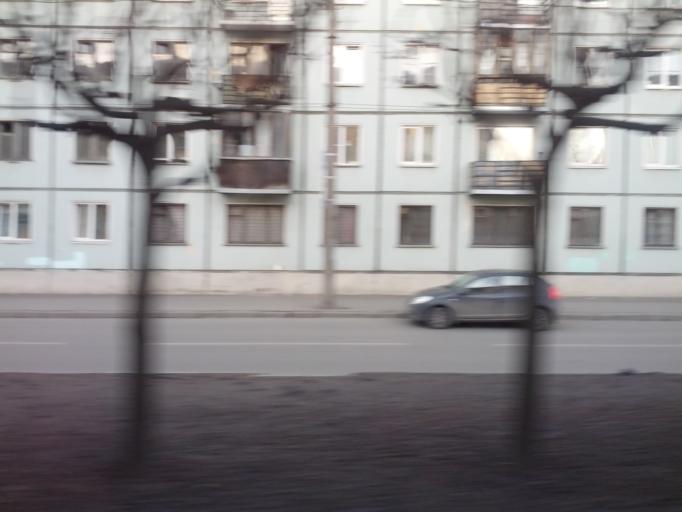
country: RU
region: St.-Petersburg
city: Centralniy
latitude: 59.9215
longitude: 30.4209
